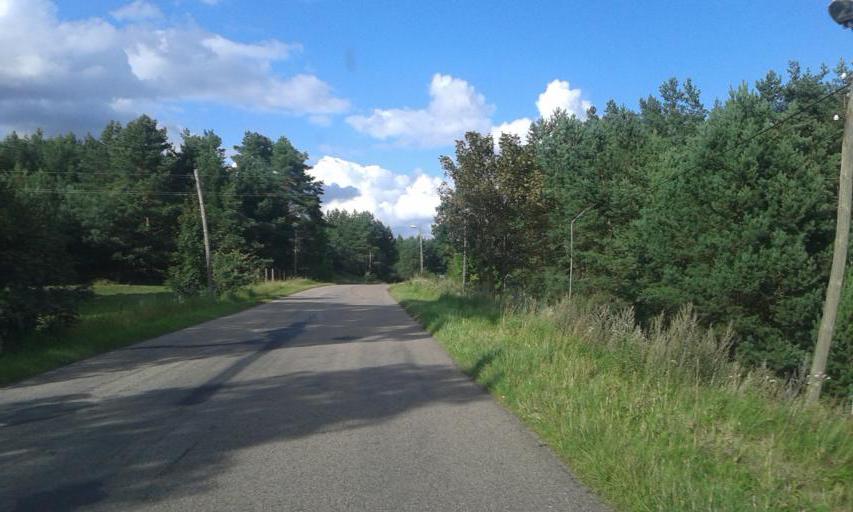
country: PL
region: West Pomeranian Voivodeship
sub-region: Powiat szczecinecki
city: Barwice
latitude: 53.6524
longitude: 16.3157
